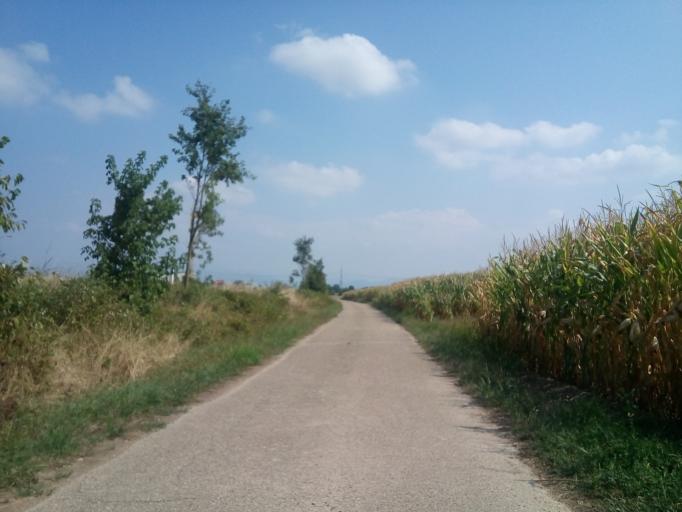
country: DE
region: Baden-Wuerttemberg
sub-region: Freiburg Region
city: Rheinau
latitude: 48.6336
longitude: 7.9119
